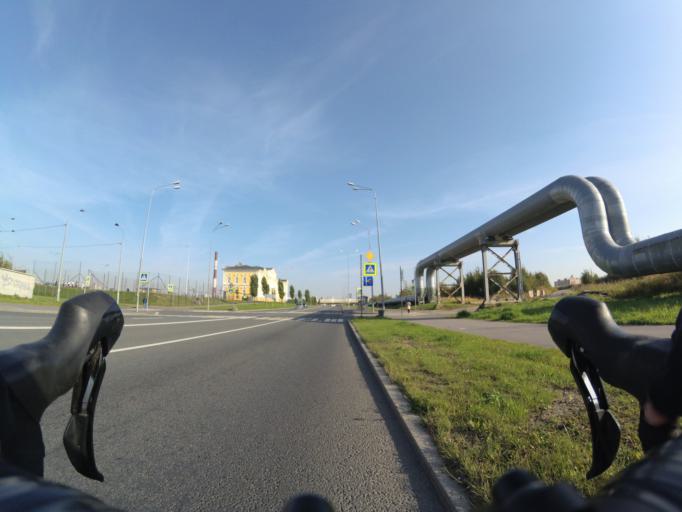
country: RU
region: St.-Petersburg
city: Staraya Derevnya
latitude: 59.9932
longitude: 30.2239
